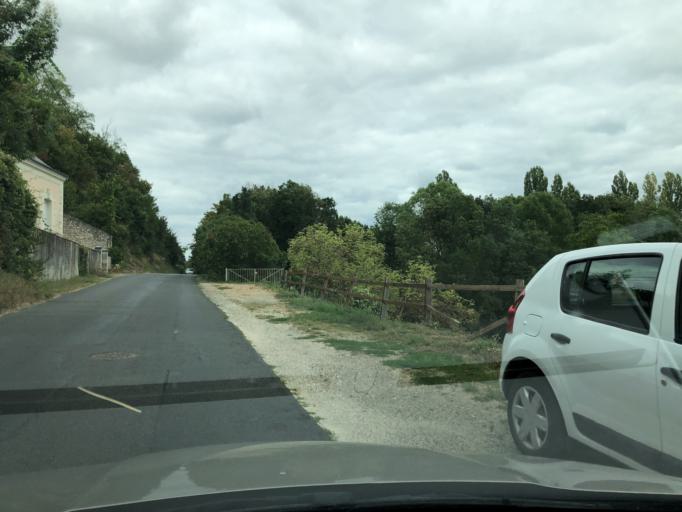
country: FR
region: Centre
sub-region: Departement d'Indre-et-Loire
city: Saint-Etienne-de-Chigny
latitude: 47.3740
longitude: 0.5270
